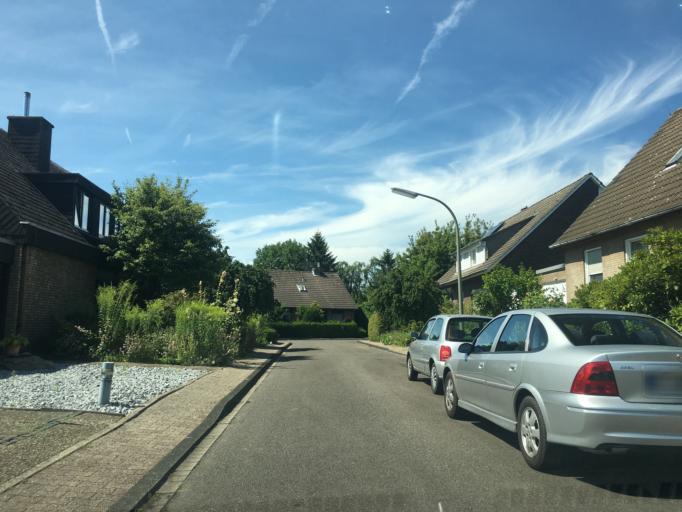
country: DE
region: North Rhine-Westphalia
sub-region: Regierungsbezirk Munster
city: Altenberge
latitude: 52.0480
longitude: 7.4606
